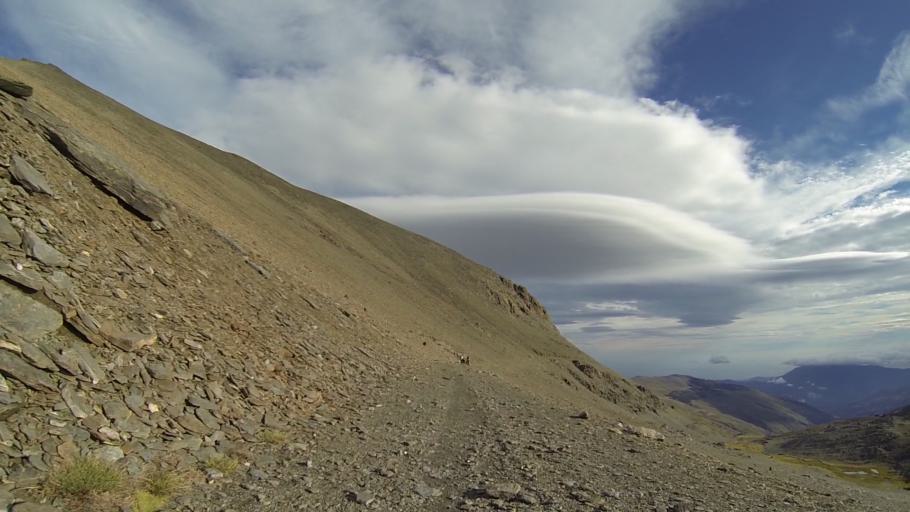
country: ES
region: Andalusia
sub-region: Provincia de Granada
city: Trevelez
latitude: 37.0525
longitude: -3.3222
